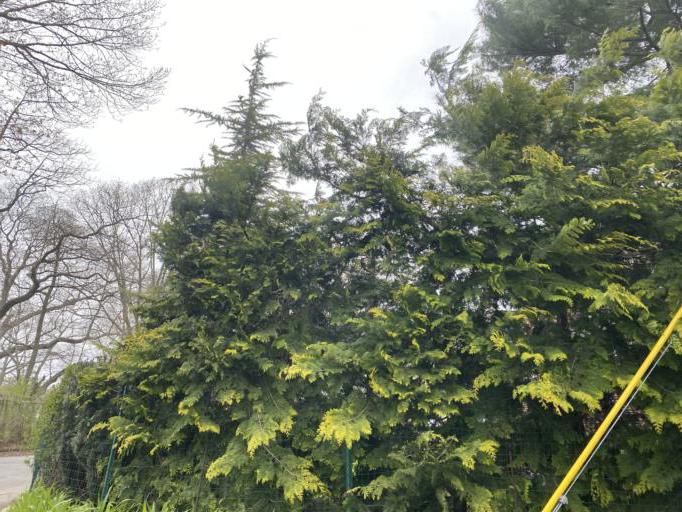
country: US
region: New York
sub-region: Nassau County
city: Floral Park
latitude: 40.7166
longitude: -73.7095
